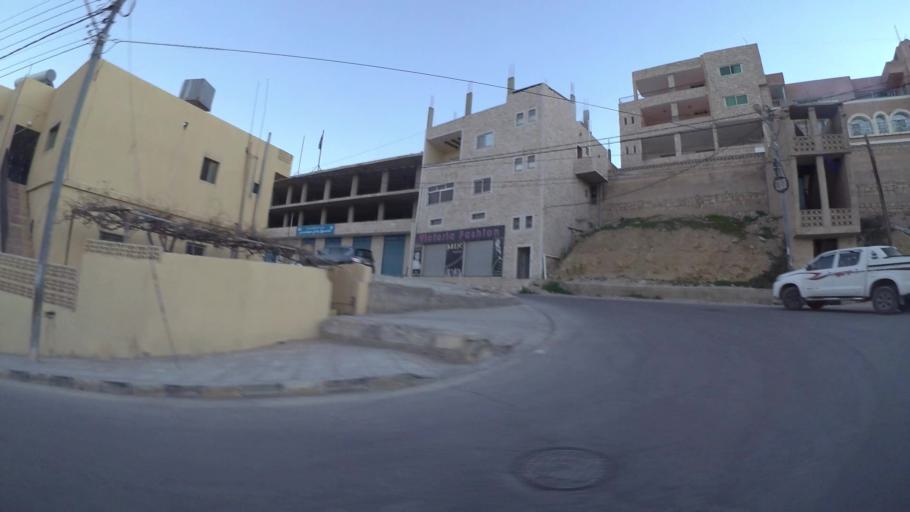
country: JO
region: Ma'an
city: Petra
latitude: 30.3207
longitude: 35.4734
